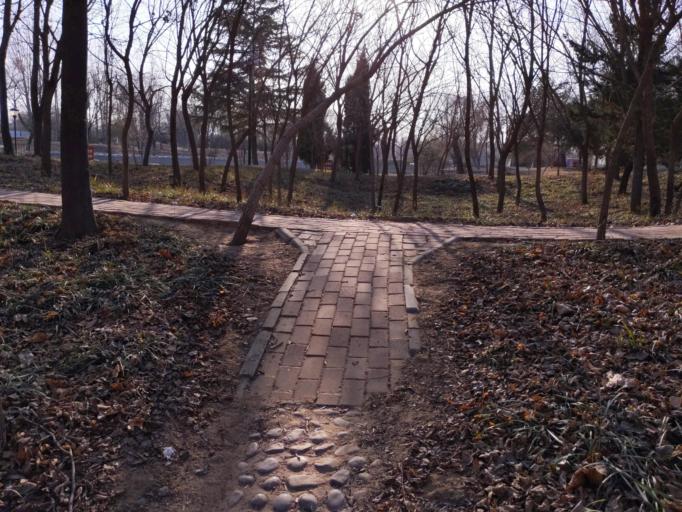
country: CN
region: Henan Sheng
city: Puyang
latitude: 35.7780
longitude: 114.9591
